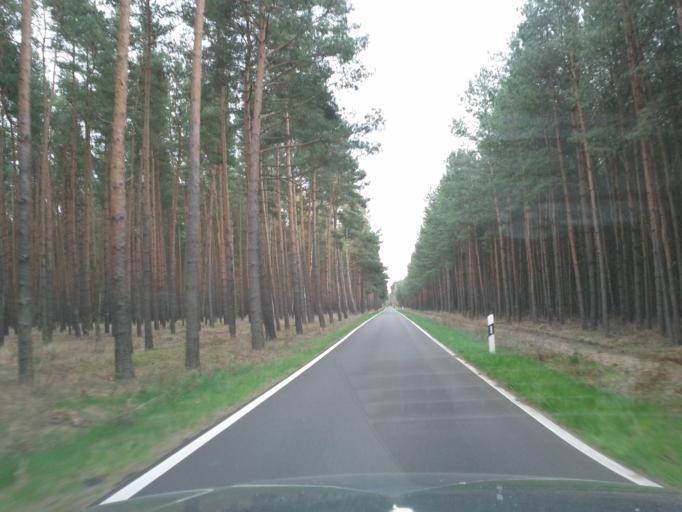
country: DE
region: Brandenburg
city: Spreenhagen
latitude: 52.3912
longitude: 13.8494
